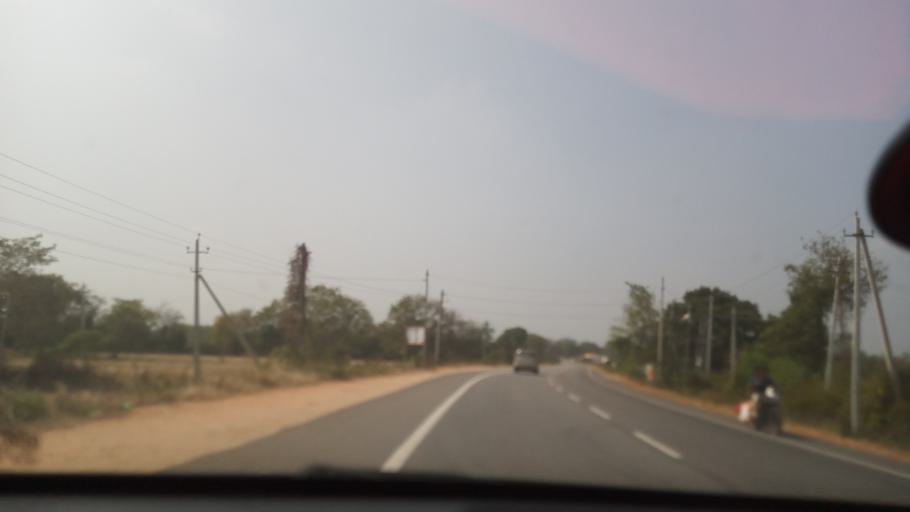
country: IN
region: Karnataka
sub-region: Mysore
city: Nanjangud
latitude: 12.0649
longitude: 76.7539
